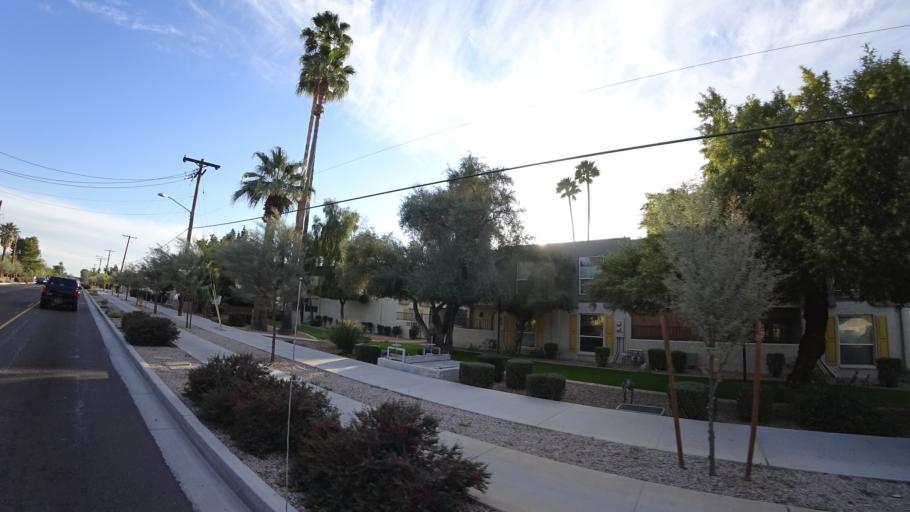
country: US
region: Arizona
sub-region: Maricopa County
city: Tempe Junction
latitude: 33.4143
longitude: -111.9522
